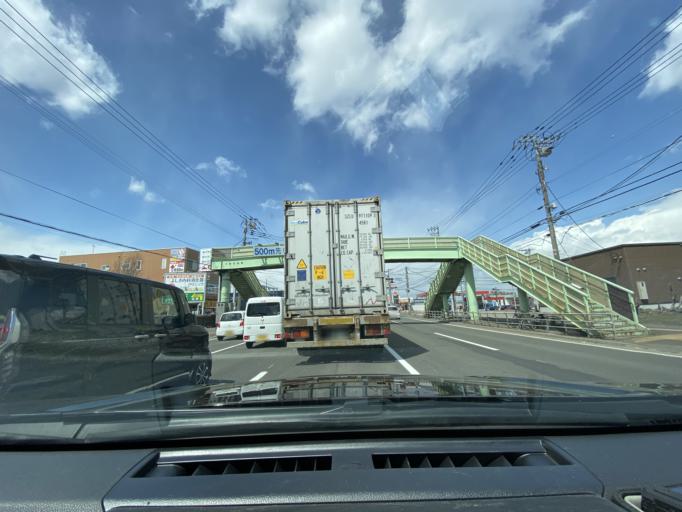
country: JP
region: Hokkaido
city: Kitahiroshima
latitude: 42.9714
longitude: 141.4777
